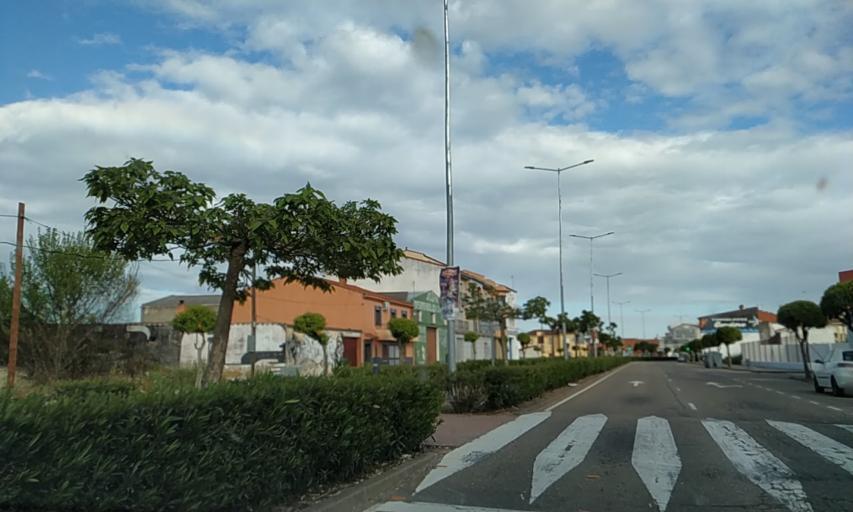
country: ES
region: Extremadura
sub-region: Provincia de Caceres
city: Moraleja
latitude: 40.0735
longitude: -6.6614
